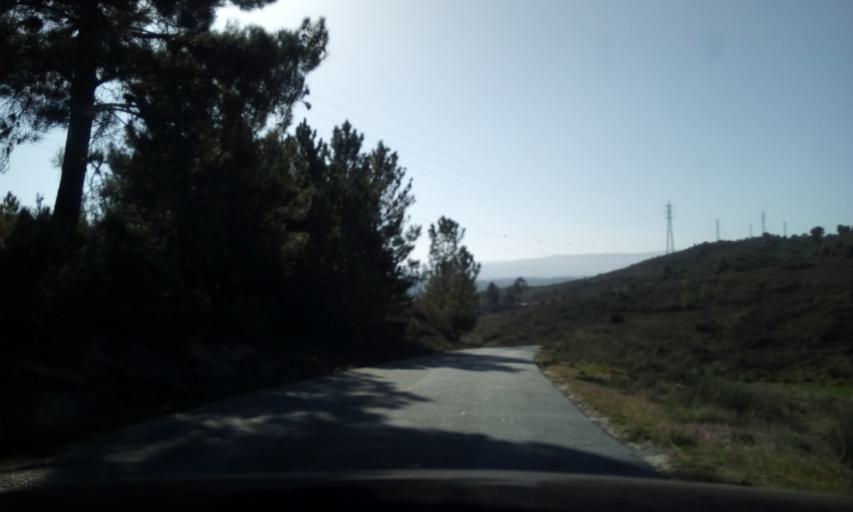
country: PT
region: Guarda
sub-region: Celorico da Beira
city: Celorico da Beira
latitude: 40.6868
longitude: -7.4161
